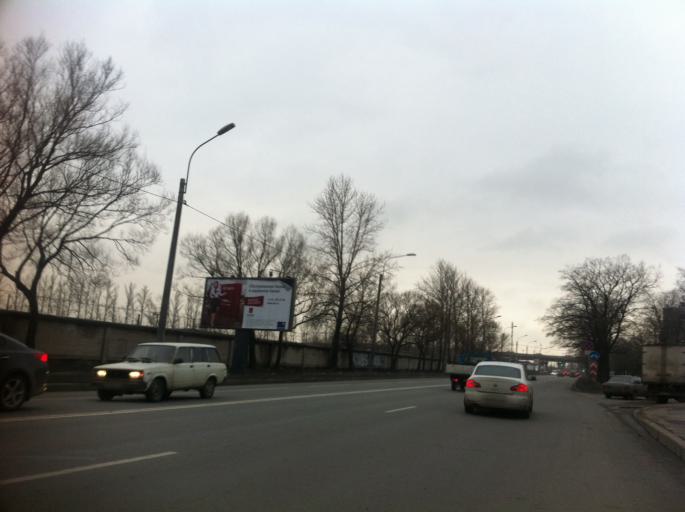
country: RU
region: St.-Petersburg
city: Dachnoye
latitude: 59.8399
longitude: 30.2727
